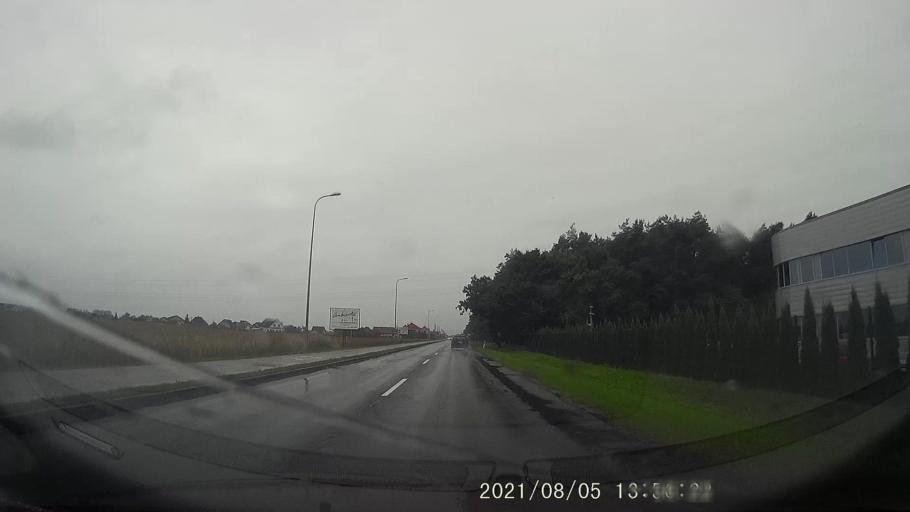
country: PL
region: Opole Voivodeship
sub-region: Powiat krapkowicki
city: Krapkowice
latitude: 50.4638
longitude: 17.9456
